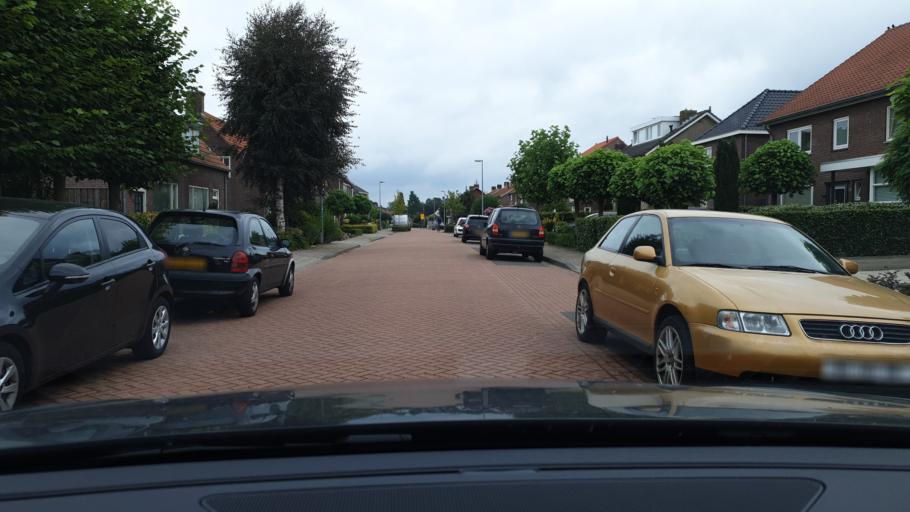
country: NL
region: North Brabant
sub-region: Gemeente Veldhoven
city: Veldhoven
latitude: 51.4219
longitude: 5.4140
